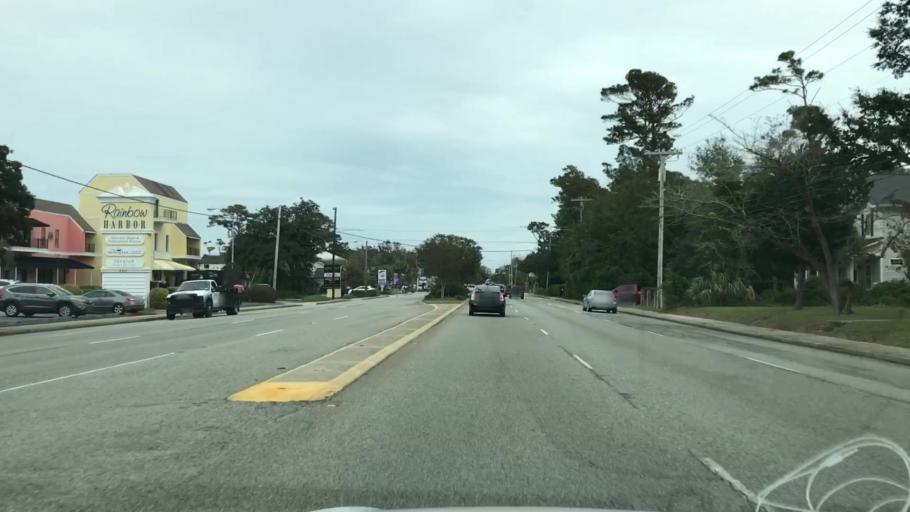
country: US
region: South Carolina
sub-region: Horry County
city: Myrtle Beach
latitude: 33.7244
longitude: -78.8457
